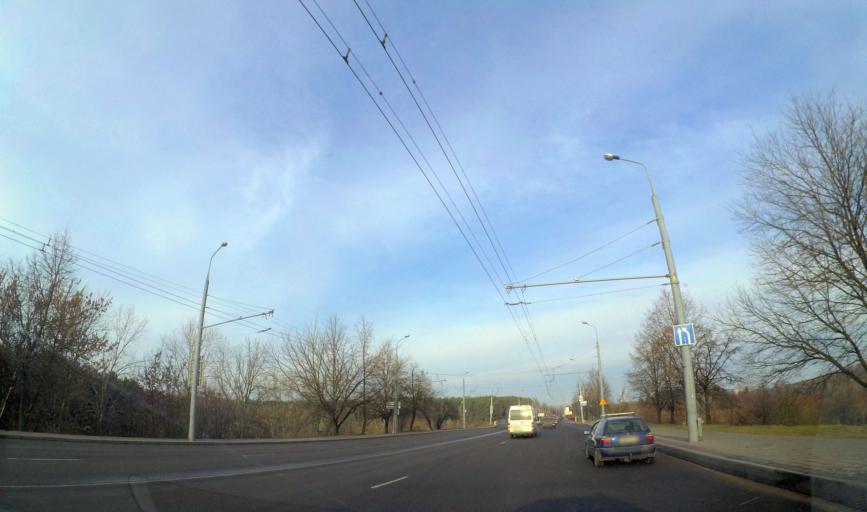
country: BY
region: Grodnenskaya
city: Hrodna
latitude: 53.6770
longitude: 23.8055
